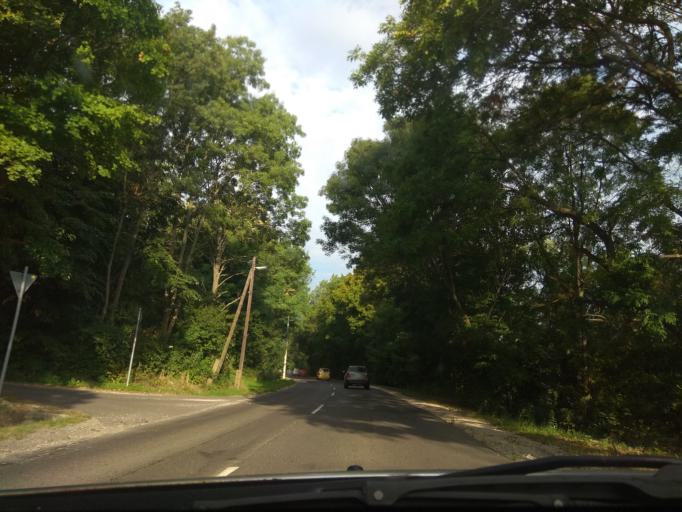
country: HU
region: Borsod-Abauj-Zemplen
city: Miskolc
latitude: 48.0874
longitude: 20.7365
